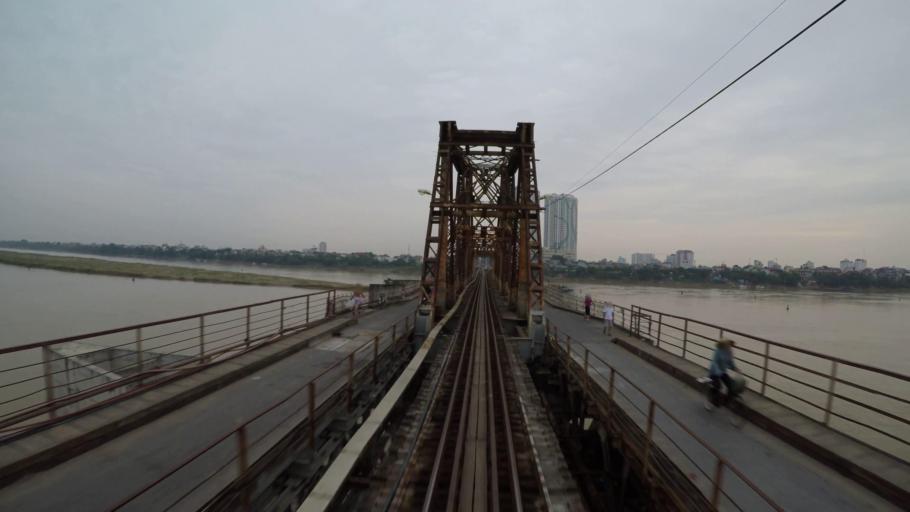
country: VN
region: Ha Noi
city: Hoan Kiem
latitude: 21.0538
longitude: 105.8828
